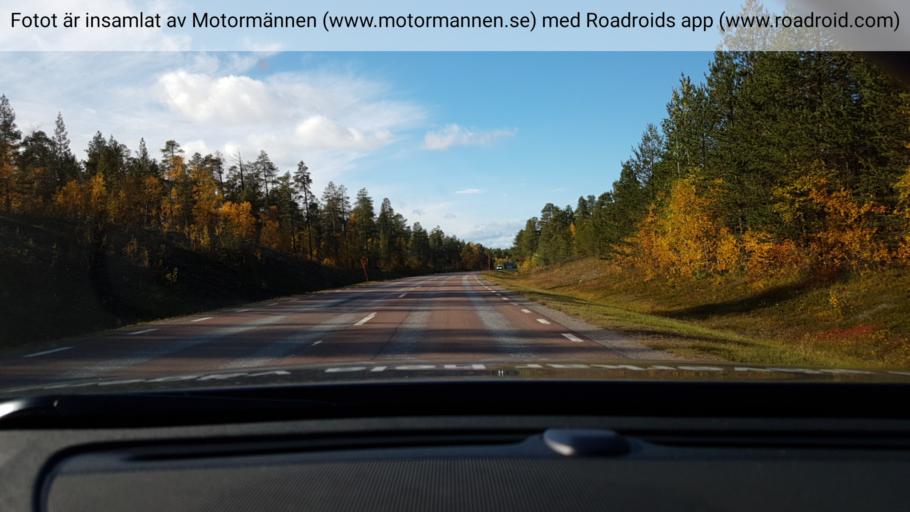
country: SE
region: Norrbotten
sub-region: Arjeplogs Kommun
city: Arjeplog
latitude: 66.0528
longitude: 17.9174
